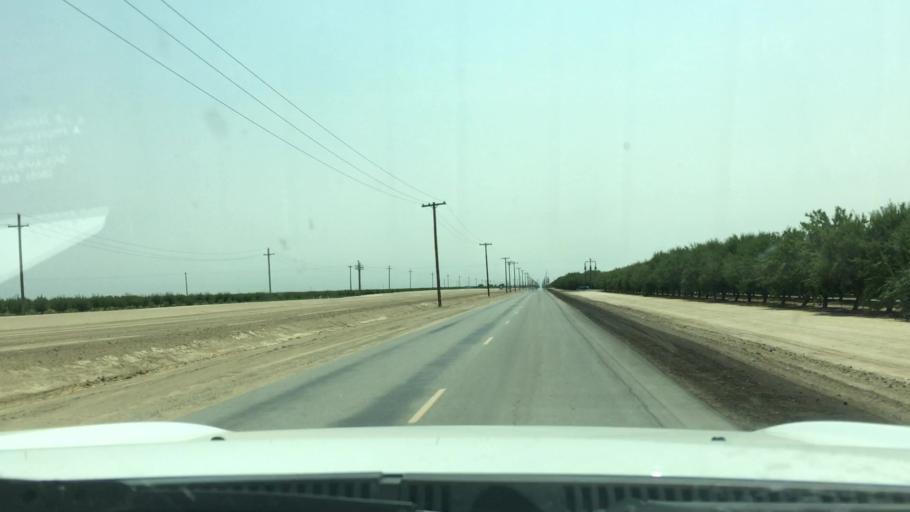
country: US
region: California
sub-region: Kern County
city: Wasco
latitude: 35.6258
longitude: -119.4378
